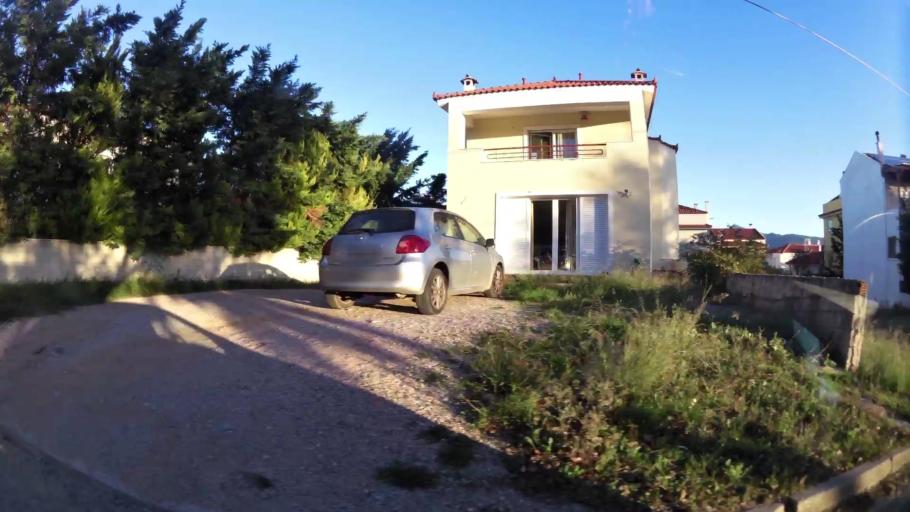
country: GR
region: Attica
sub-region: Nomarchia Anatolikis Attikis
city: Kryoneri
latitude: 38.1459
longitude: 23.8289
